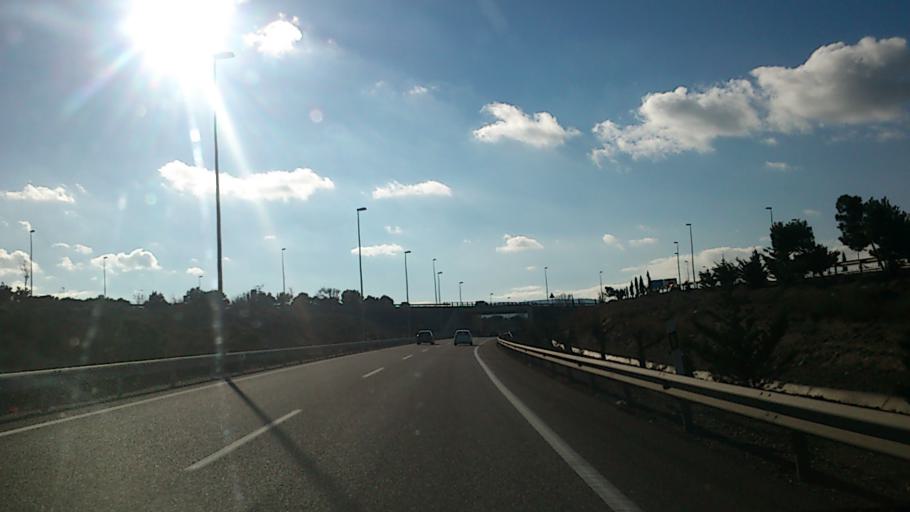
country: ES
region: Aragon
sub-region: Provincia de Zaragoza
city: Montecanal
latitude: 41.6364
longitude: -0.9753
